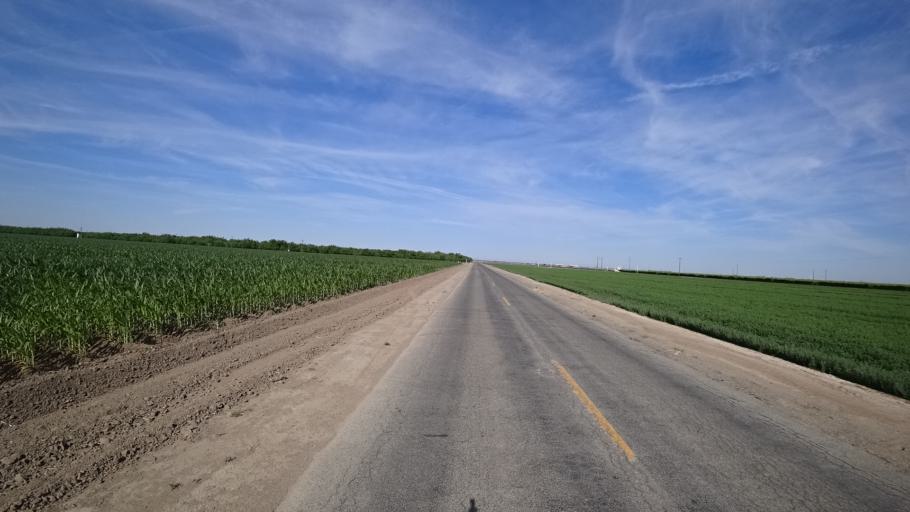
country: US
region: California
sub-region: Tulare County
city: Goshen
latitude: 36.3491
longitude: -119.4814
